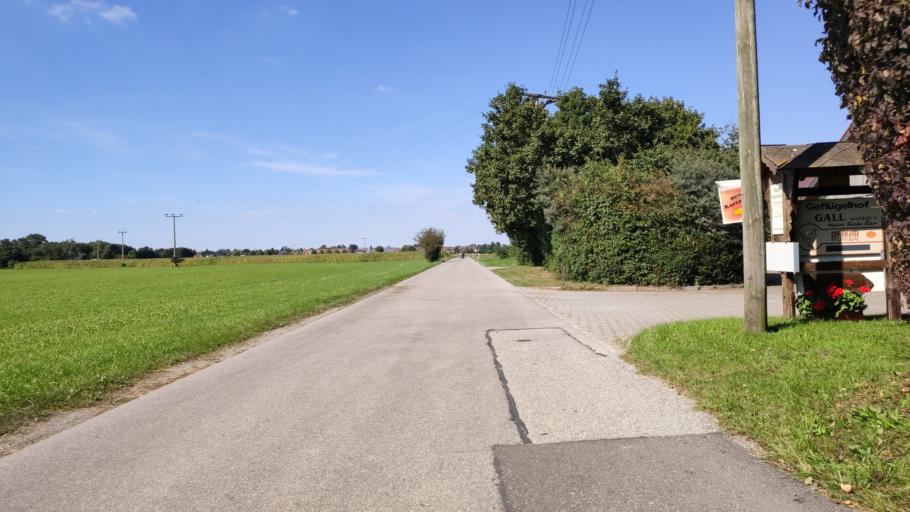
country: DE
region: Bavaria
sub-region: Swabia
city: Konigsbrunn
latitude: 48.2447
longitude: 10.9032
